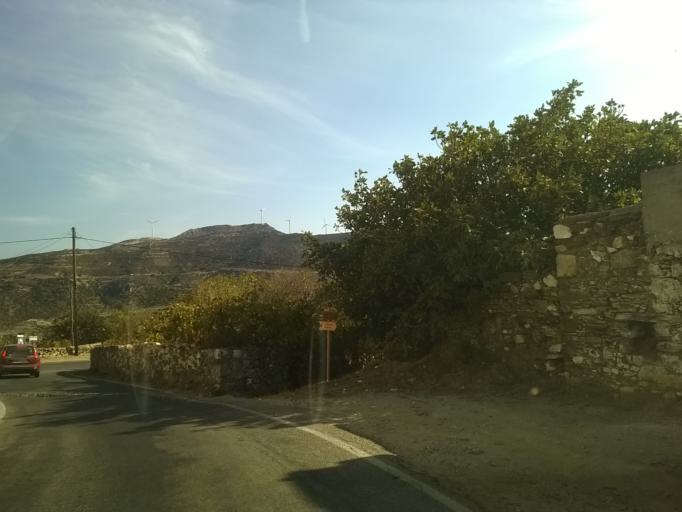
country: GR
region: South Aegean
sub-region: Nomos Kykladon
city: Filotion
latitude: 37.1267
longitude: 25.5392
